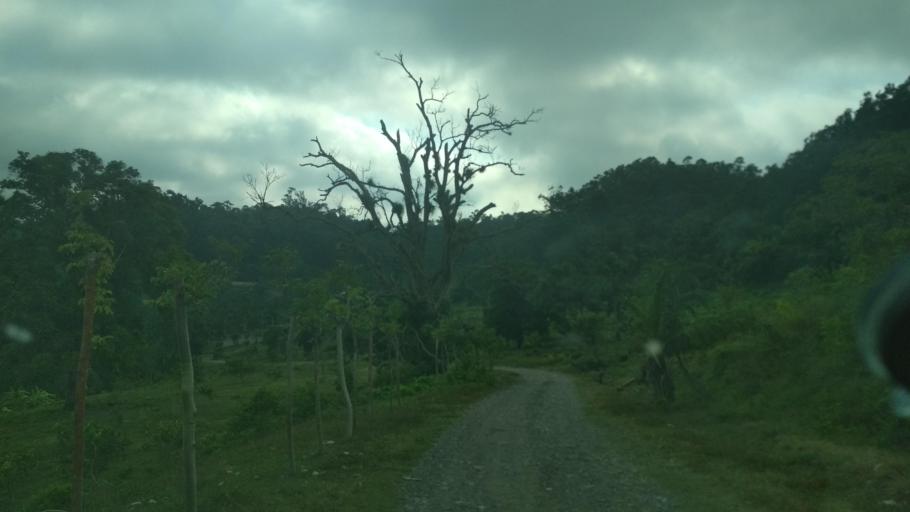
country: MX
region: Veracruz
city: Papantla de Olarte
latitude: 20.4748
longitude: -97.3531
